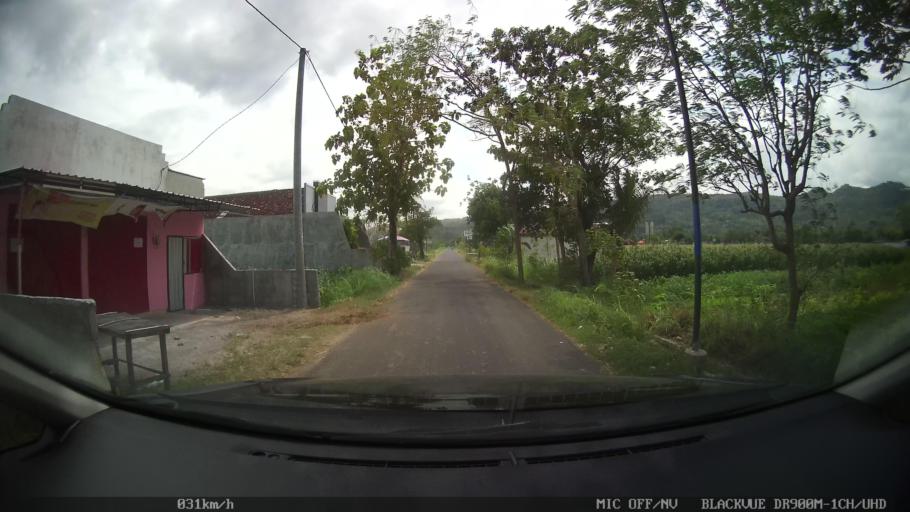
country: ID
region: Central Java
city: Candi Prambanan
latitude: -7.8112
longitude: 110.5002
